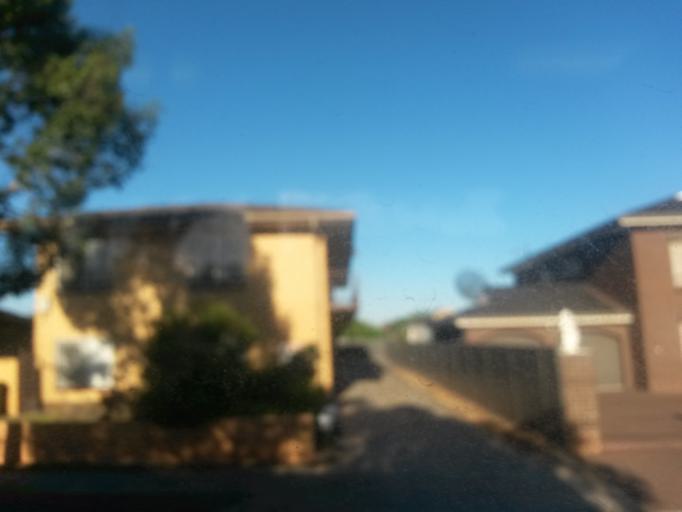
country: AU
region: South Australia
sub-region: Charles Sturt
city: Woodville
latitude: -34.8819
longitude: 138.5667
